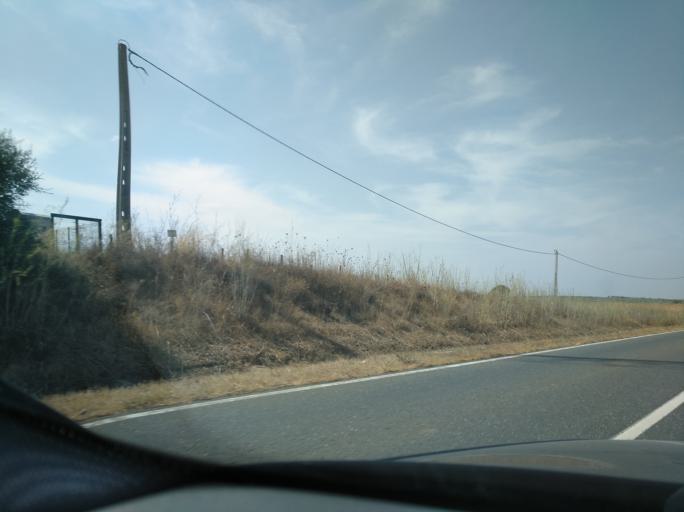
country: PT
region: Beja
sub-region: Beja
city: Beja
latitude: 37.8562
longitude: -7.8599
